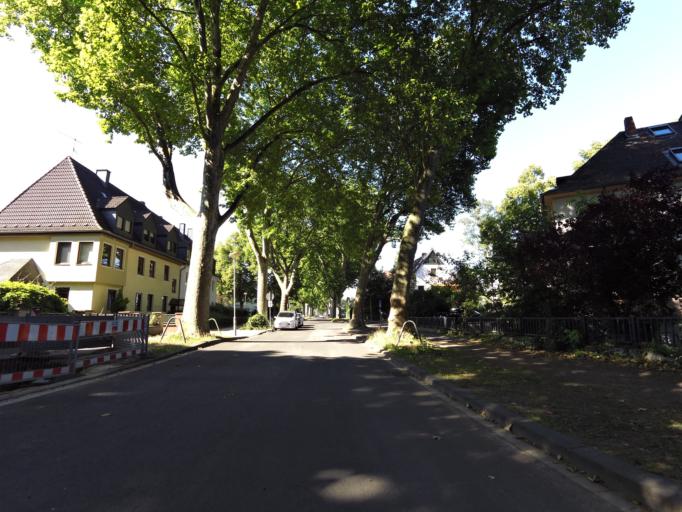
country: DE
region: Rheinland-Pfalz
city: Koblenz
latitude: 50.3350
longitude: 7.5897
